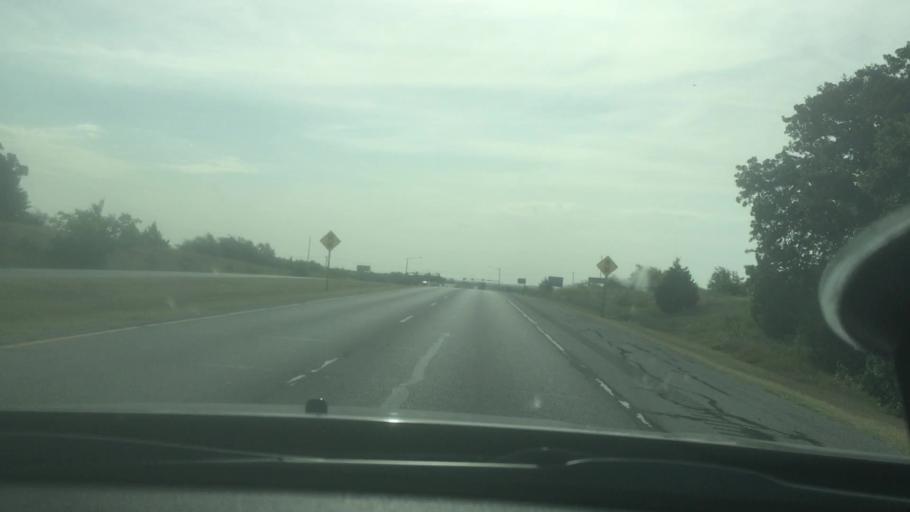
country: US
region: Oklahoma
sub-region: Carter County
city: Ardmore
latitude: 34.1392
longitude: -97.1471
